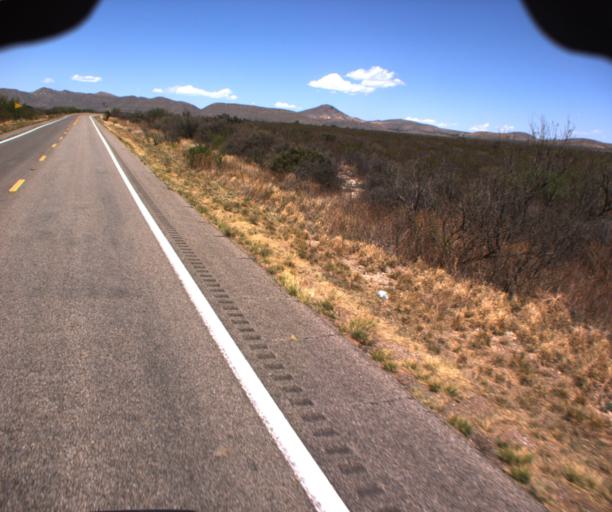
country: US
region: Arizona
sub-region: Cochise County
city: Tombstone
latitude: 31.6125
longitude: -110.0511
